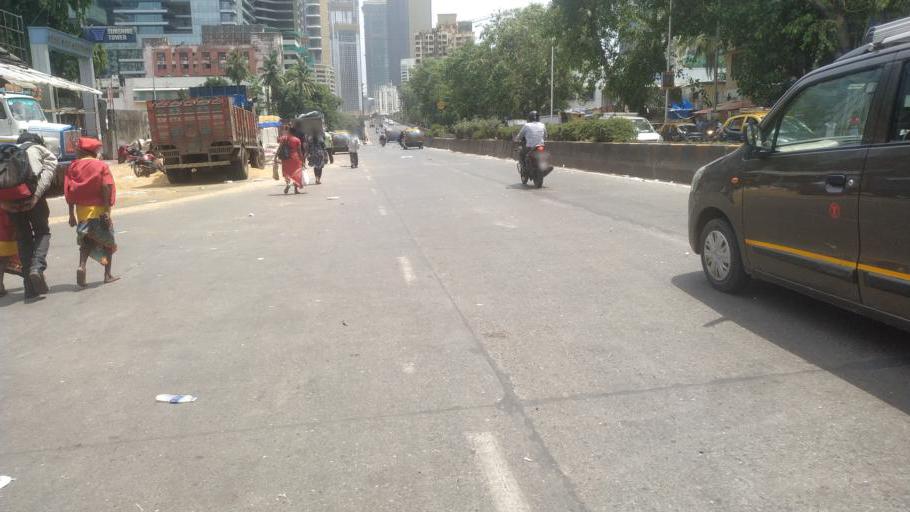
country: IN
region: Maharashtra
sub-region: Mumbai Suburban
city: Mumbai
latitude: 19.0126
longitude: 72.8367
